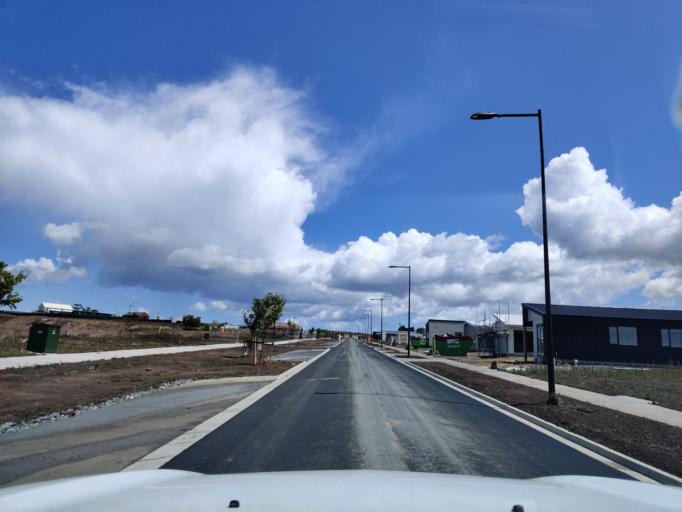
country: NZ
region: Waikato
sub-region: Waikato District
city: Te Kauwhata
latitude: -37.4122
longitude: 175.1516
